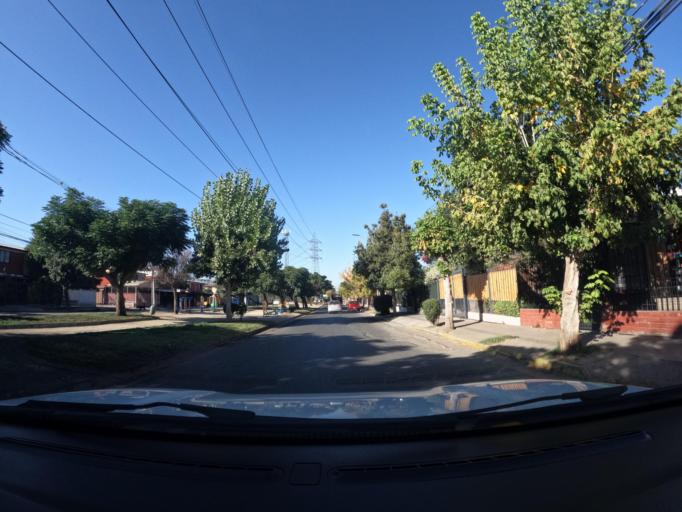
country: CL
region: Santiago Metropolitan
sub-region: Provincia de Santiago
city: Villa Presidente Frei, Nunoa, Santiago, Chile
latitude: -33.5051
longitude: -70.5747
